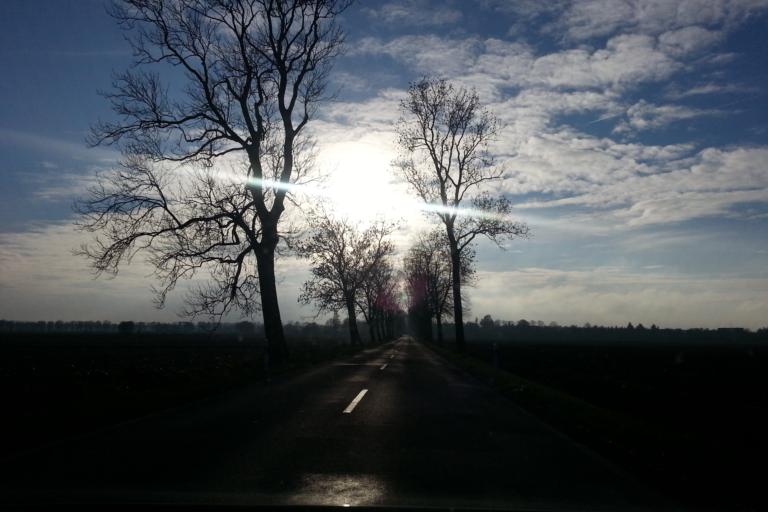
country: DE
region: Mecklenburg-Vorpommern
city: Ferdinandshof
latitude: 53.6497
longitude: 13.8676
